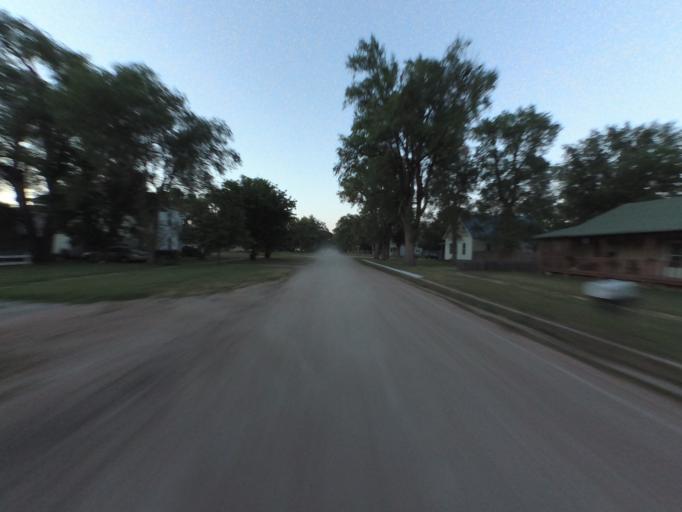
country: US
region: Kansas
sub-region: Reno County
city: Nickerson
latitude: 38.1417
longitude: -98.0857
